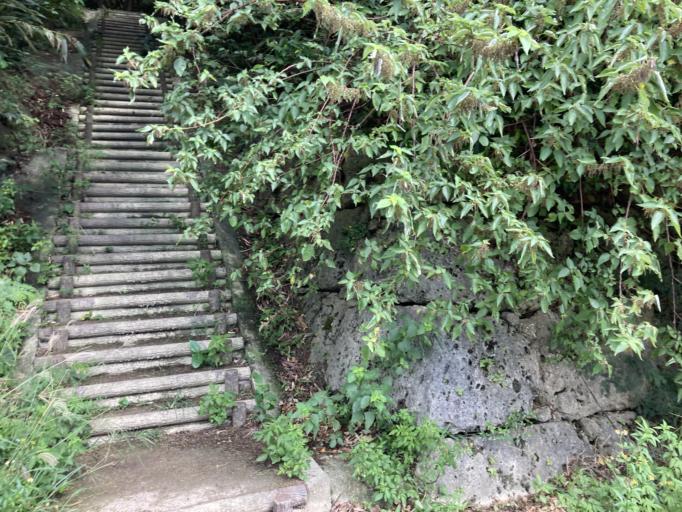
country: JP
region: Okinawa
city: Ginowan
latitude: 26.1665
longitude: 127.8284
